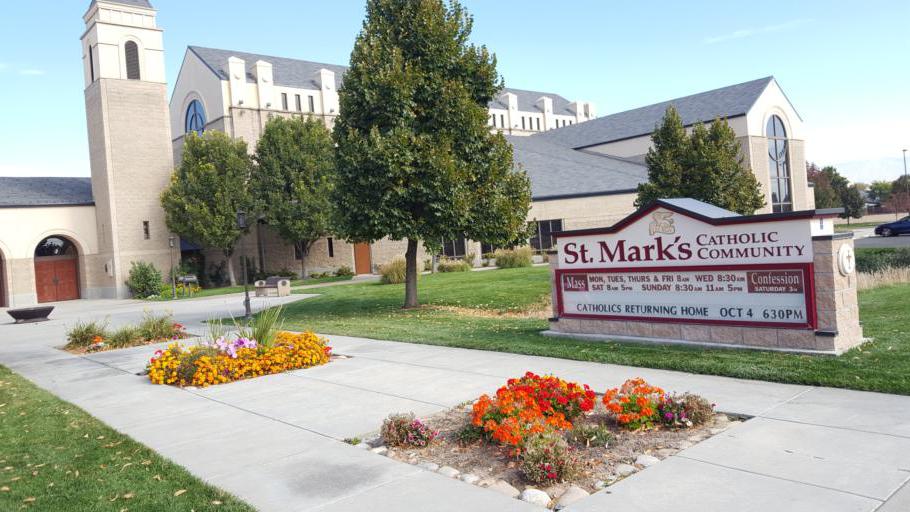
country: US
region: Idaho
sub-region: Ada County
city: Garden City
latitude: 43.6272
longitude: -116.2800
